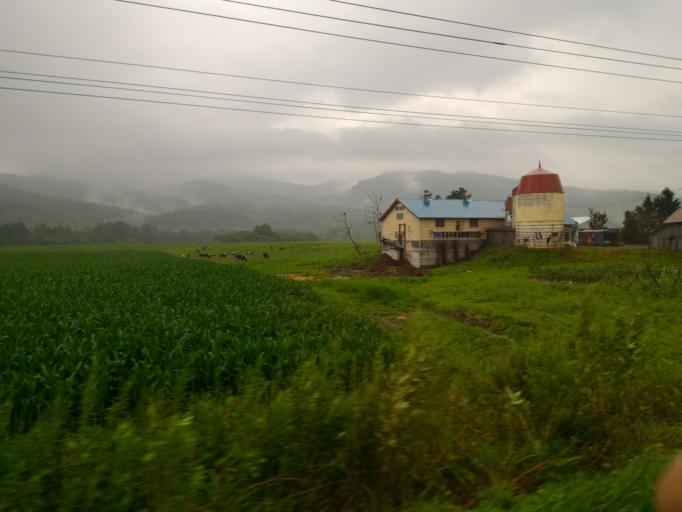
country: JP
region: Hokkaido
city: Nayoro
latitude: 44.5750
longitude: 142.3120
